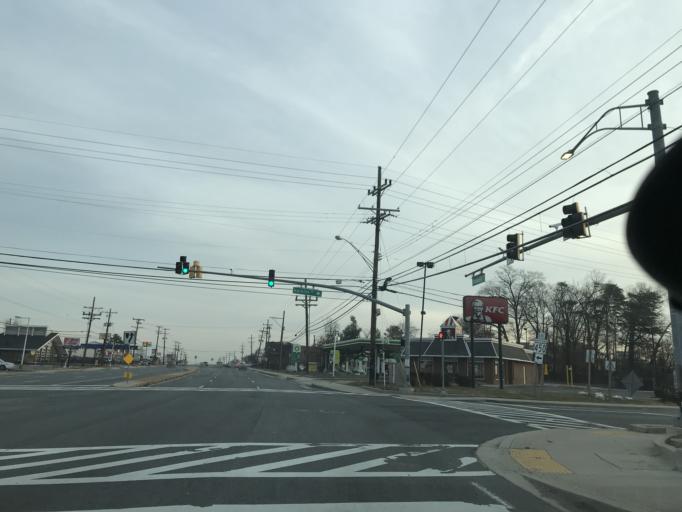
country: US
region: Maryland
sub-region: Prince George's County
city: Woodlawn
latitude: 38.9526
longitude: -76.8789
